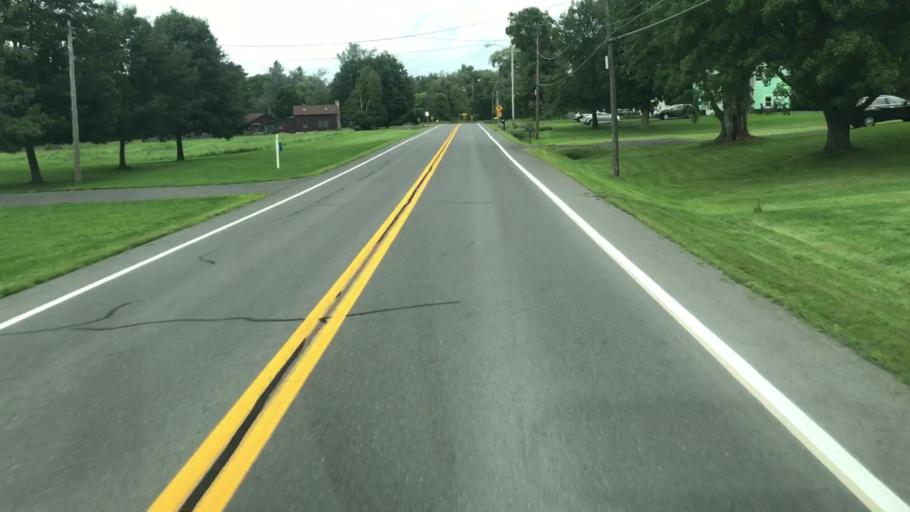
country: US
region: New York
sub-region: Onondaga County
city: Elbridge
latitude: 43.0046
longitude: -76.4574
